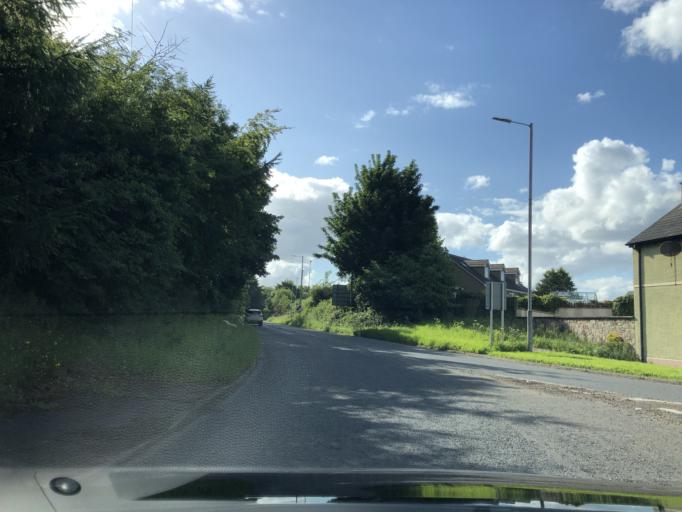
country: GB
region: Northern Ireland
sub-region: Ards District
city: Comber
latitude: 54.5470
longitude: -5.7430
